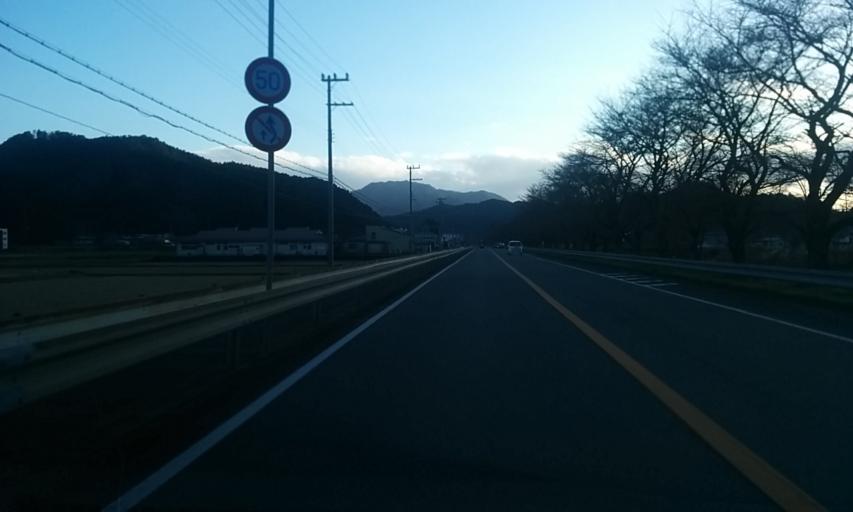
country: JP
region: Hyogo
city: Sasayama
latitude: 35.1044
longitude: 135.3178
